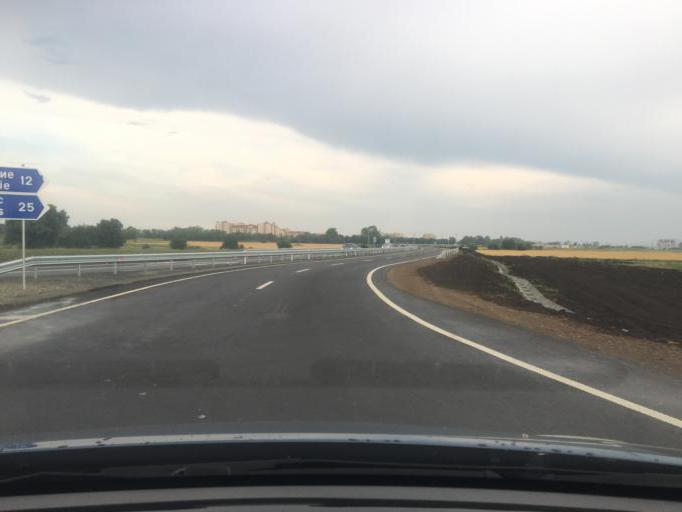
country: BG
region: Burgas
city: Aheloy
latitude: 42.6456
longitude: 27.6366
